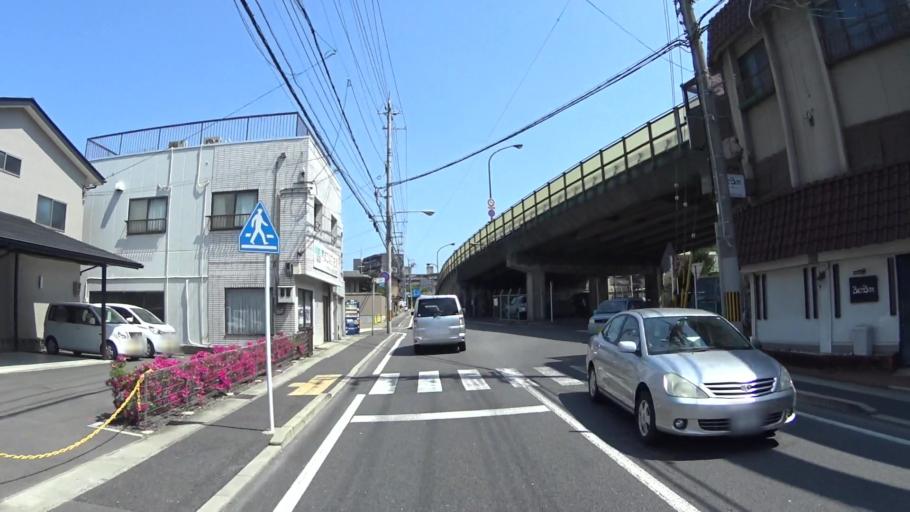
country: JP
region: Kyoto
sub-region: Kyoto-shi
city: Kamigyo-ku
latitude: 35.0562
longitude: 135.7916
